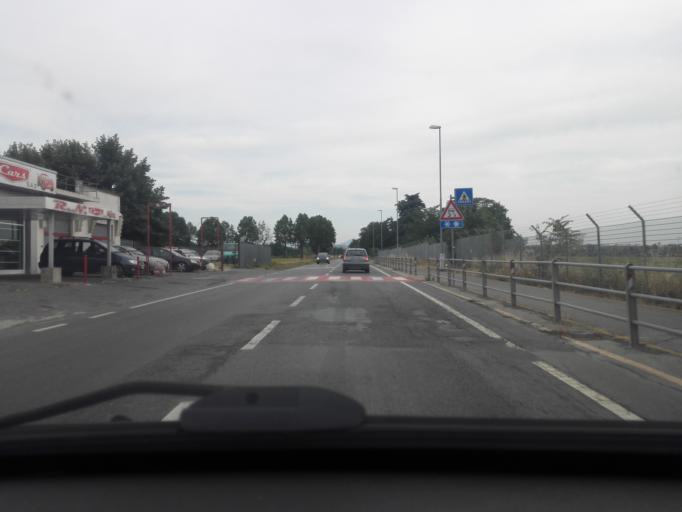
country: IT
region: Piedmont
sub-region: Provincia di Alessandria
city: Novi Ligure
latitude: 44.7819
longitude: 8.7891
